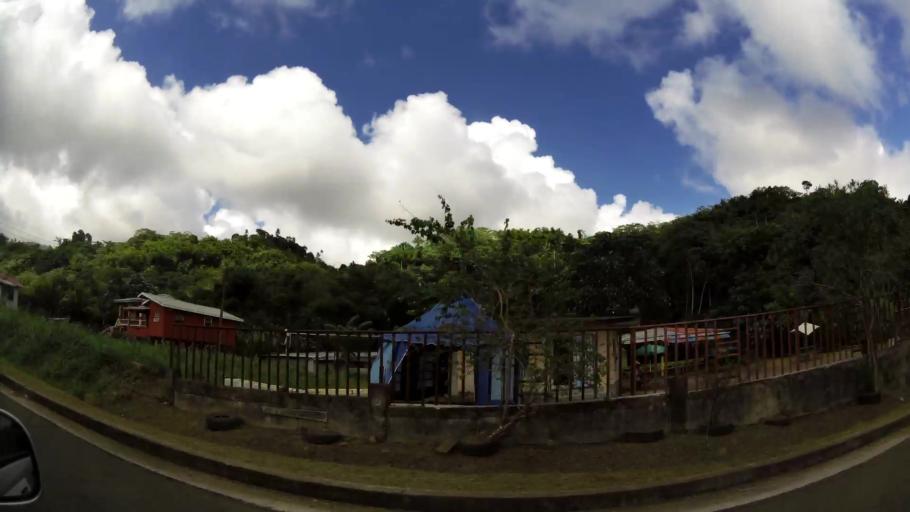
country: GD
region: Saint Andrew
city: Grenville
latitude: 12.1284
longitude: -61.6562
